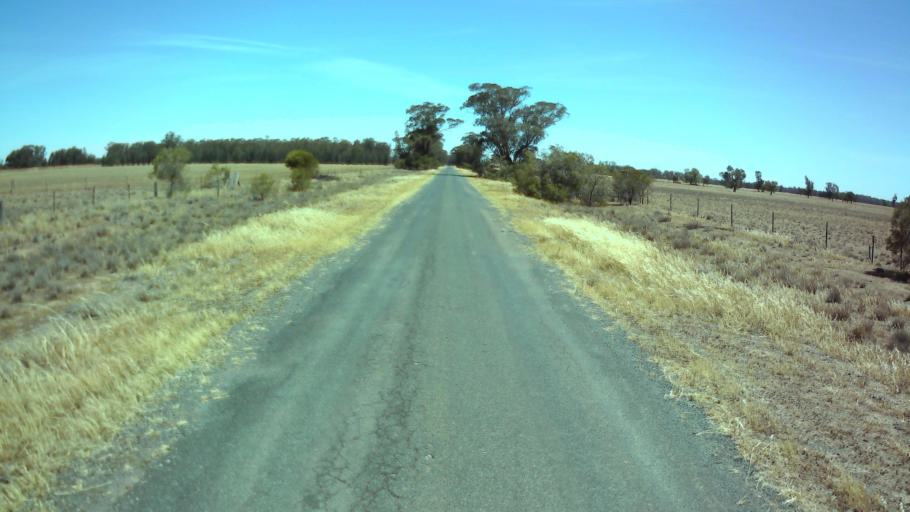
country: AU
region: New South Wales
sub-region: Weddin
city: Grenfell
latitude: -33.8991
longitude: 147.6867
